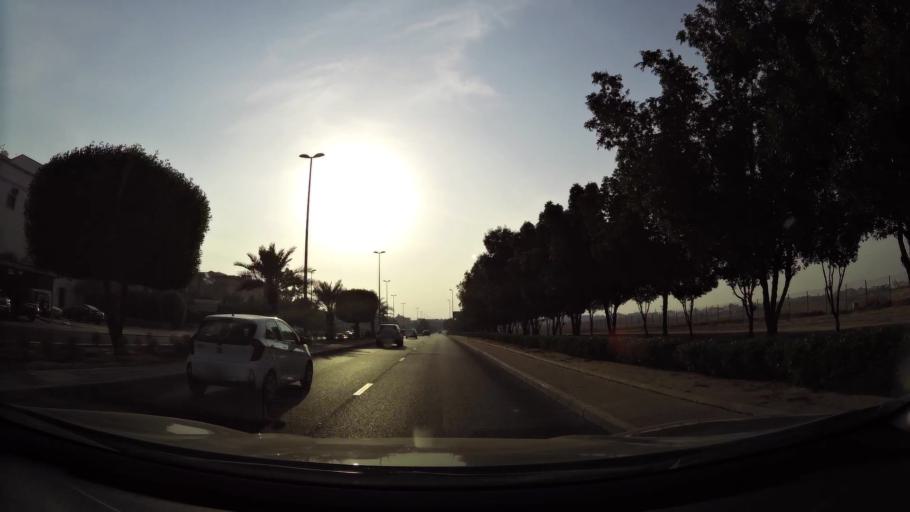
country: KW
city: Al Funaytis
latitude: 29.2222
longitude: 48.0767
